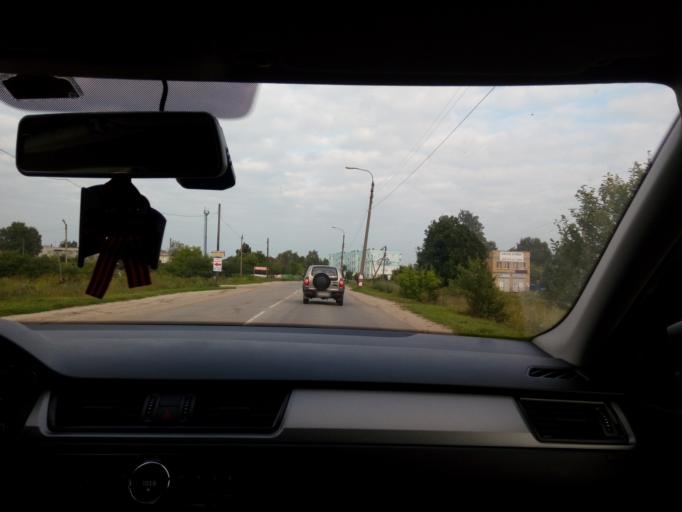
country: RU
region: Nizjnij Novgorod
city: Voskresenskoye
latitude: 56.8384
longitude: 45.4249
